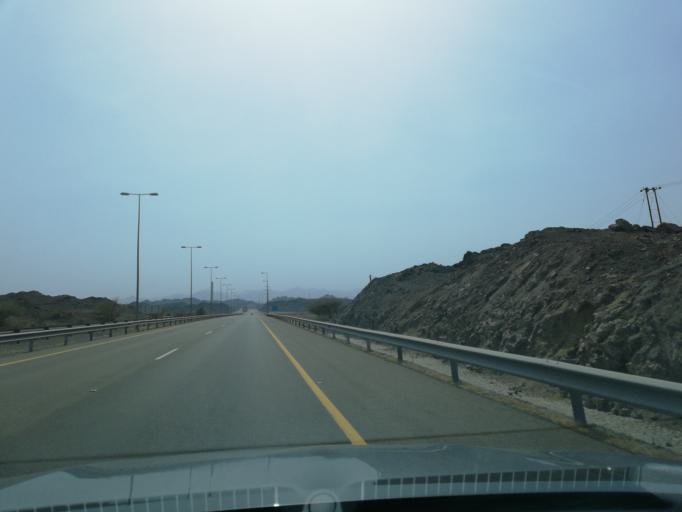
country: OM
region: Al Batinah
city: Al Liwa'
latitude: 24.3071
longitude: 56.4412
